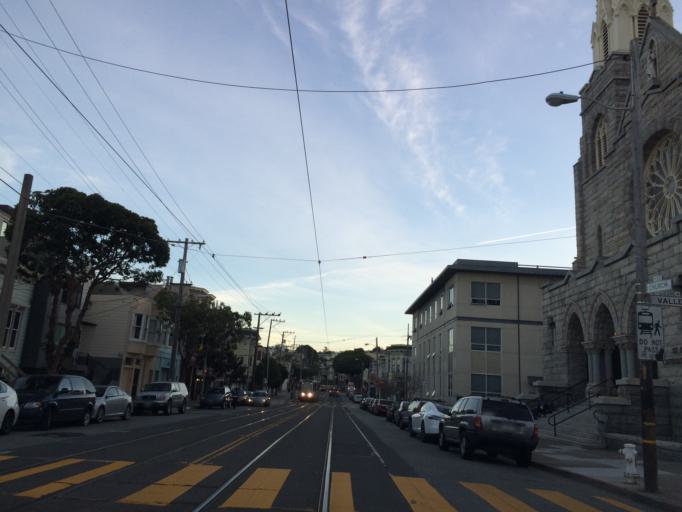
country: US
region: California
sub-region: San Francisco County
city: San Francisco
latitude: 37.7446
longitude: -122.4267
